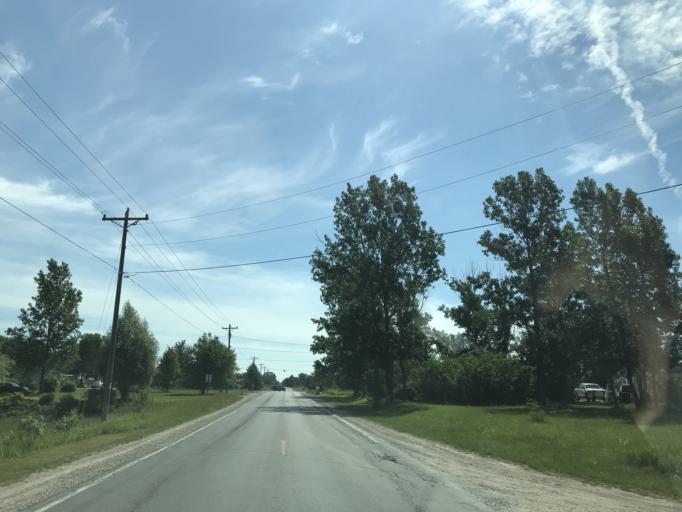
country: US
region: Michigan
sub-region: Grand Traverse County
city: Traverse City
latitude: 44.6576
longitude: -85.6786
